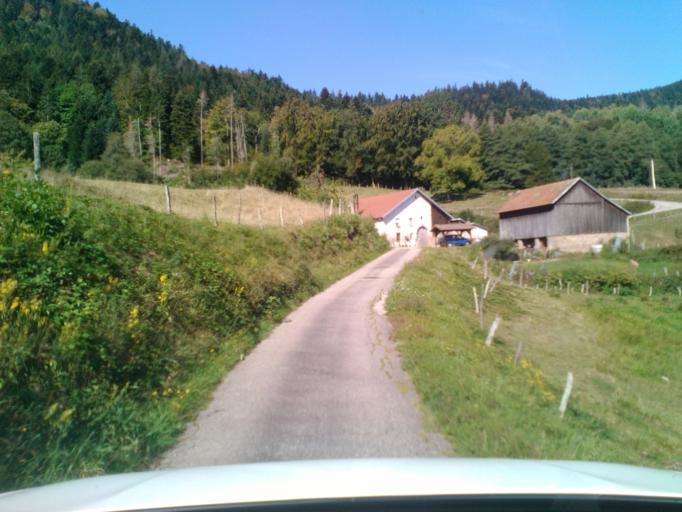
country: FR
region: Lorraine
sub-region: Departement des Vosges
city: Senones
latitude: 48.4051
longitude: 6.9804
